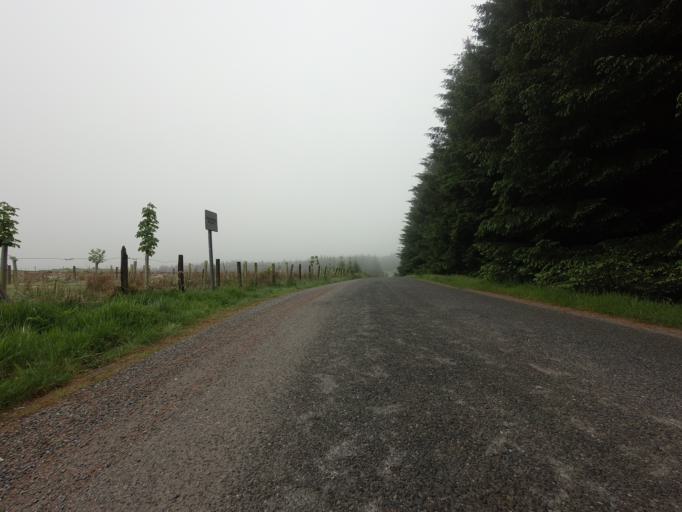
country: GB
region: Scotland
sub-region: Perth and Kinross
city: Kinross
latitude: 56.1486
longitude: -3.4523
